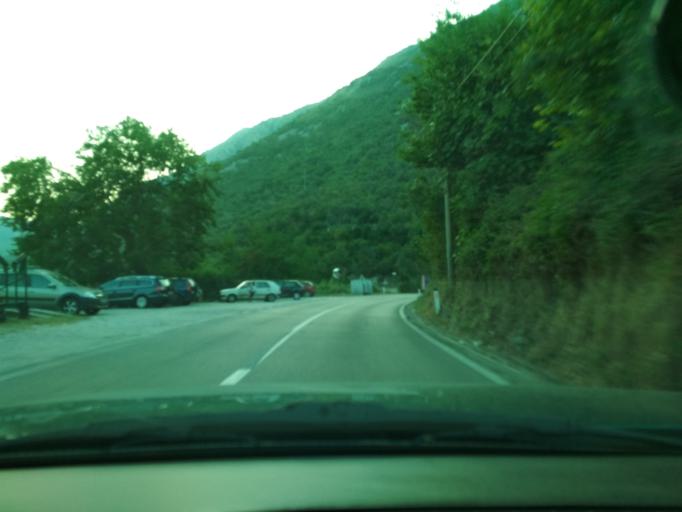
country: ME
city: Lipci
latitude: 42.5046
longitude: 18.6697
